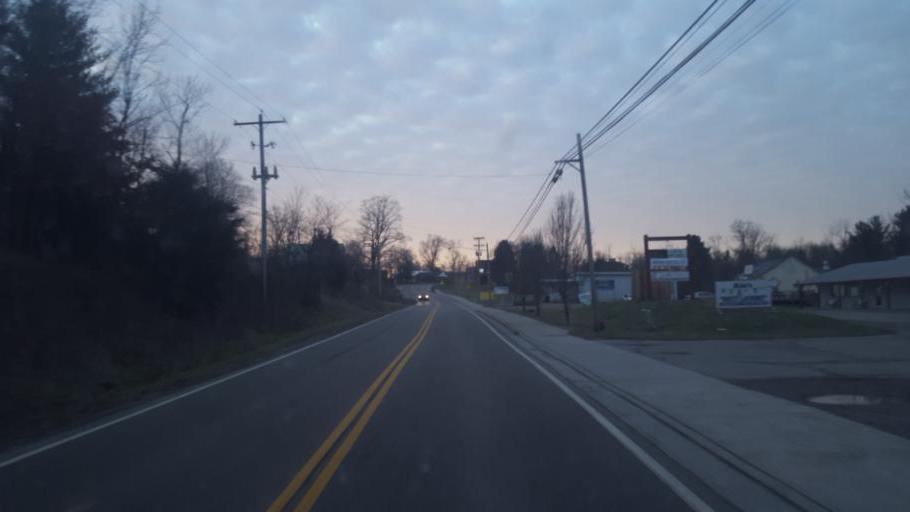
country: US
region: Ohio
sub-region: Jackson County
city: Oak Hill
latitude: 38.8857
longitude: -82.3821
